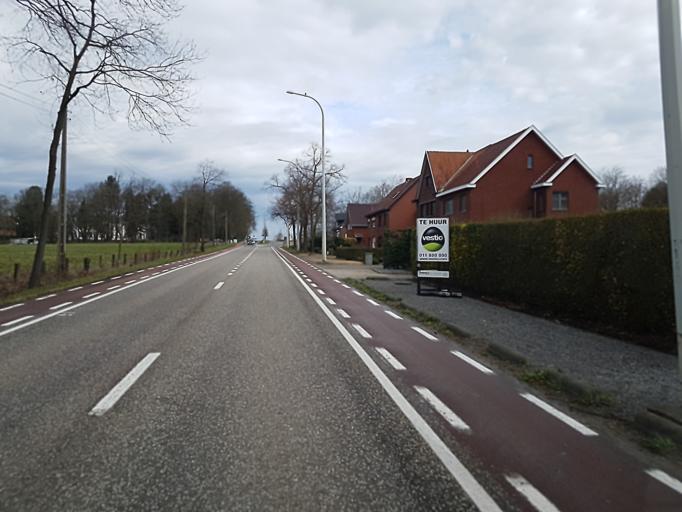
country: BE
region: Flanders
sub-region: Provincie Limburg
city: Hasselt
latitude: 50.8942
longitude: 5.3551
